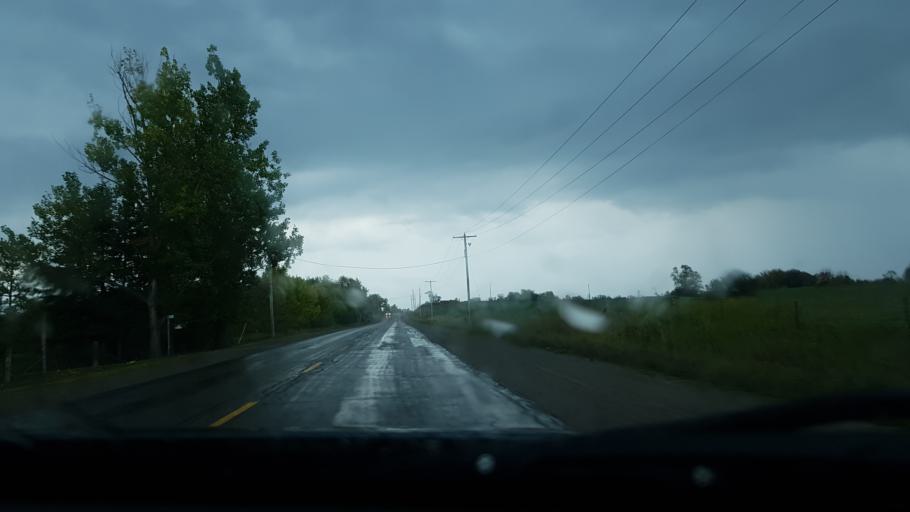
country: CA
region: Ontario
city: Omemee
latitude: 44.3675
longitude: -78.5451
